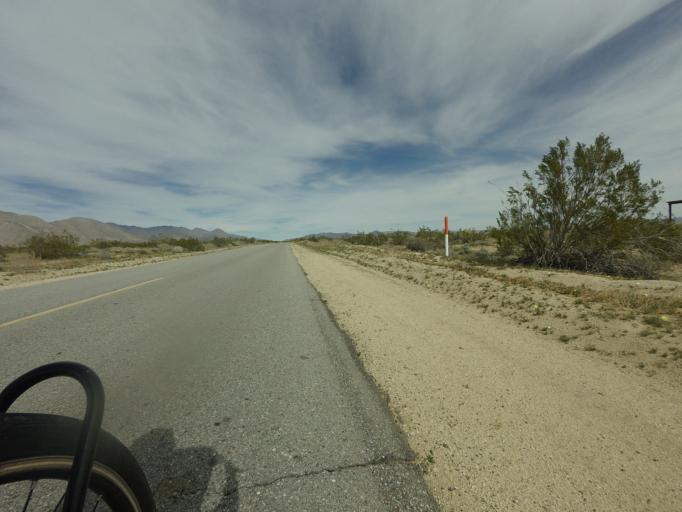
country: US
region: California
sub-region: Kern County
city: Inyokern
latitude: 35.7677
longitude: -117.8482
